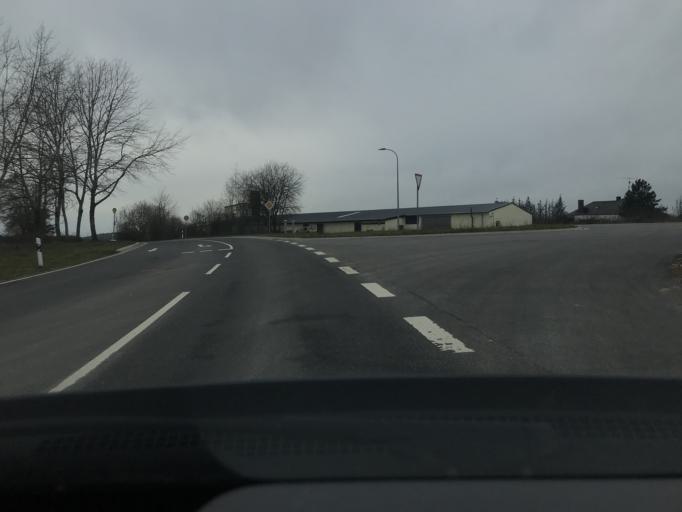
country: DE
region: Rheinland-Pfalz
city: Newel
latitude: 49.7914
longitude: 6.5637
